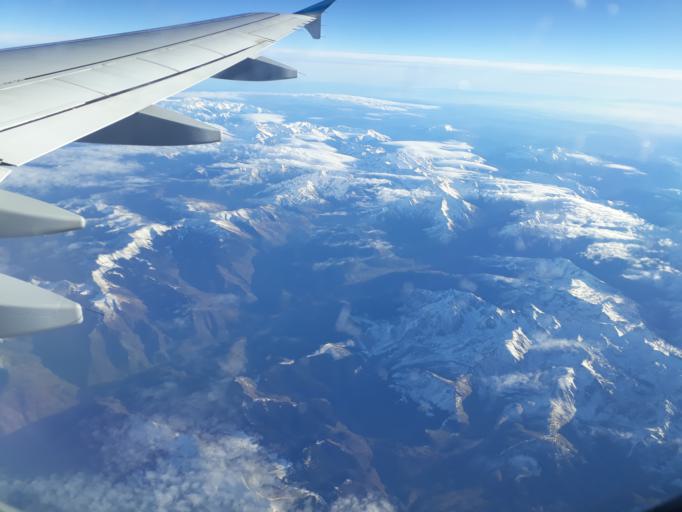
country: FR
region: Midi-Pyrenees
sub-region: Departement des Hautes-Pyrenees
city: Campan
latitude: 43.0444
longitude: 0.2168
